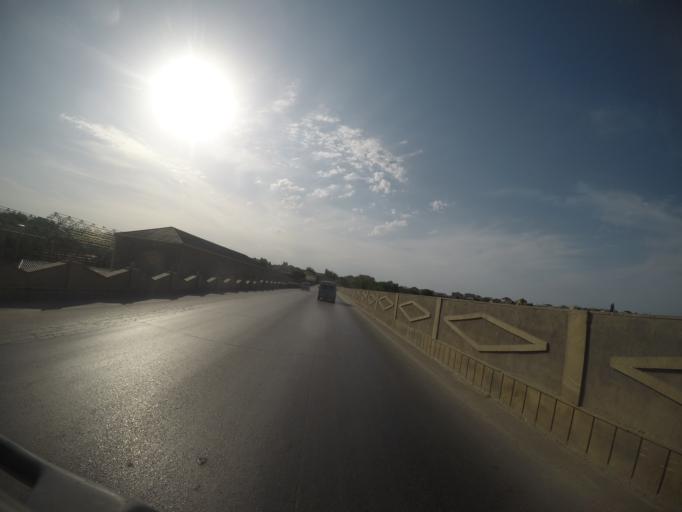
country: AZ
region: Baki
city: Binagadi
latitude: 40.4692
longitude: 49.8398
